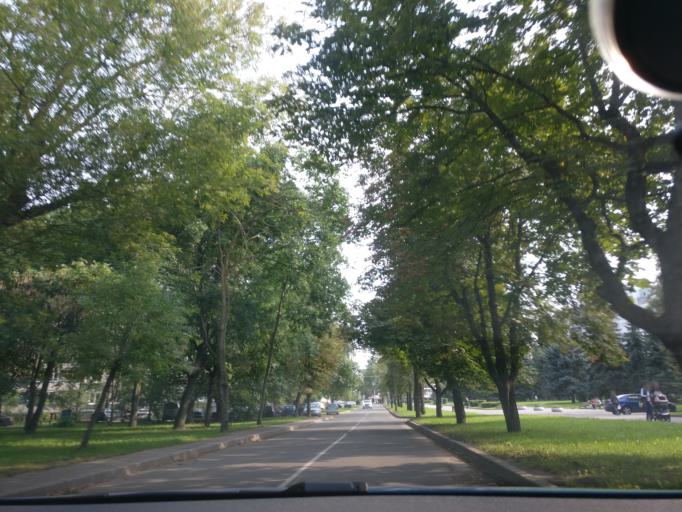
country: BY
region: Minsk
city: Minsk
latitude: 53.9246
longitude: 27.5756
